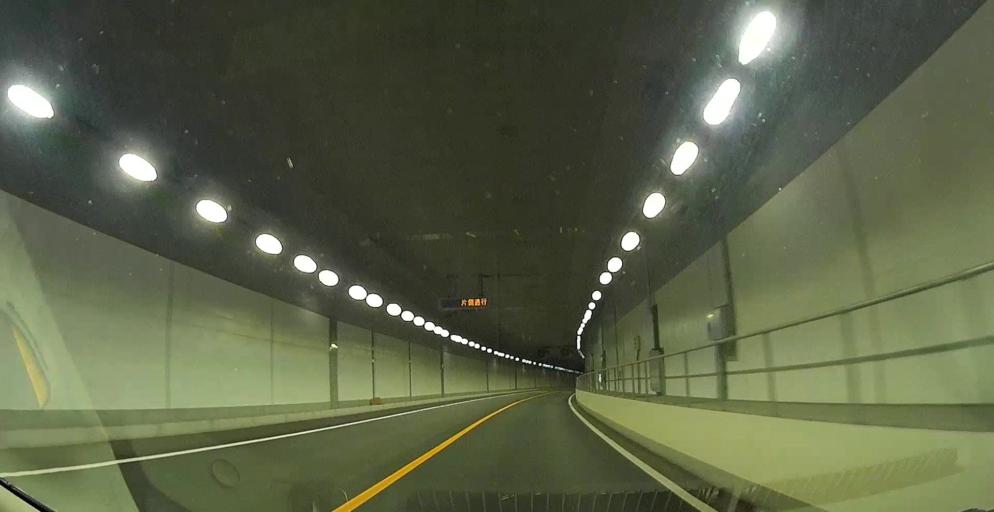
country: JP
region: Tokyo
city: Urayasu
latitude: 35.6174
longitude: 139.7950
